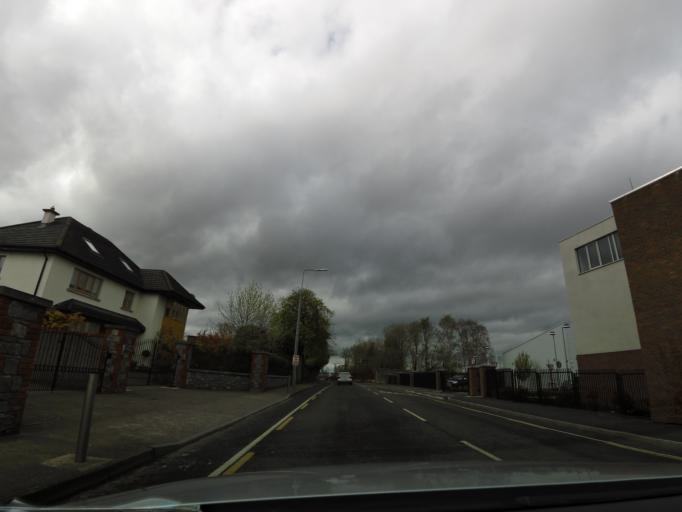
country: IE
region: Leinster
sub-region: Kilkenny
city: Kilkenny
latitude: 52.6589
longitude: -7.2618
